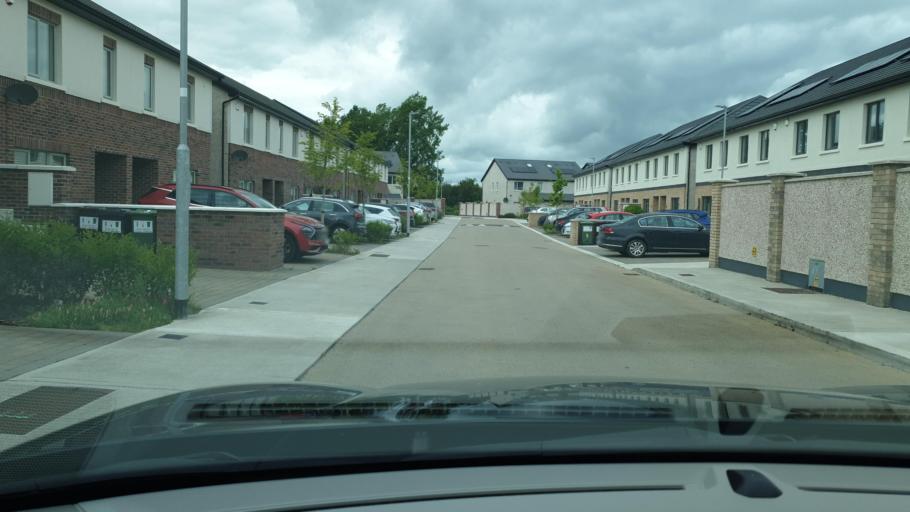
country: IE
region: Leinster
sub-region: Kildare
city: Leixlip
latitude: 53.3471
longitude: -6.4754
